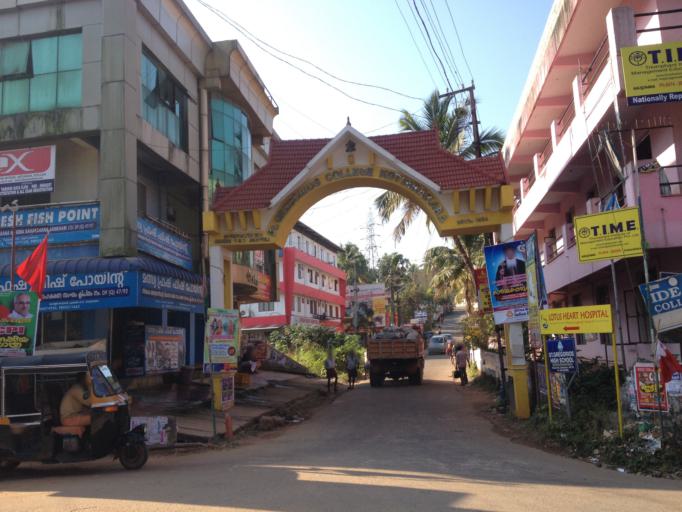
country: IN
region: Kerala
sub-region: Kollam
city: Punalur
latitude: 9.0052
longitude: 76.7856
